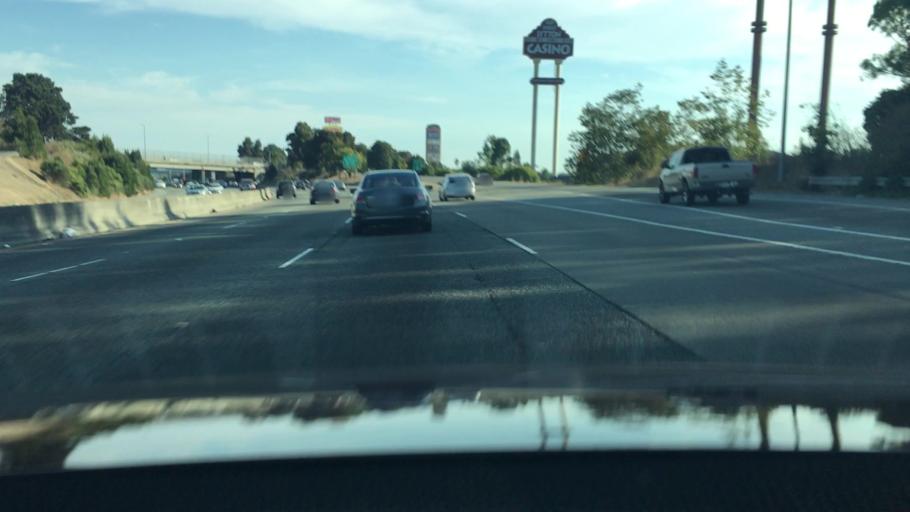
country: US
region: California
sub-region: Contra Costa County
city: Rollingwood
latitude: 37.9583
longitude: -122.3308
